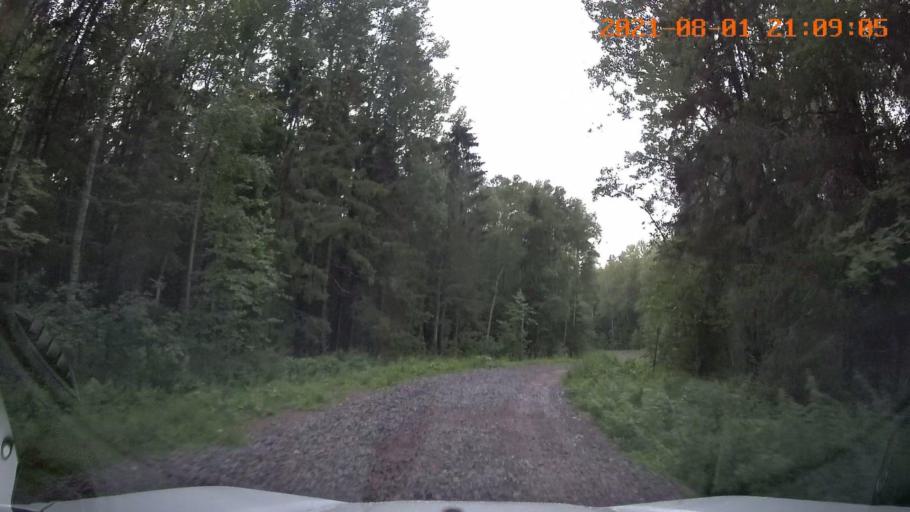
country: RU
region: Leningrad
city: Syas'stroy
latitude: 60.5103
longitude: 32.6488
